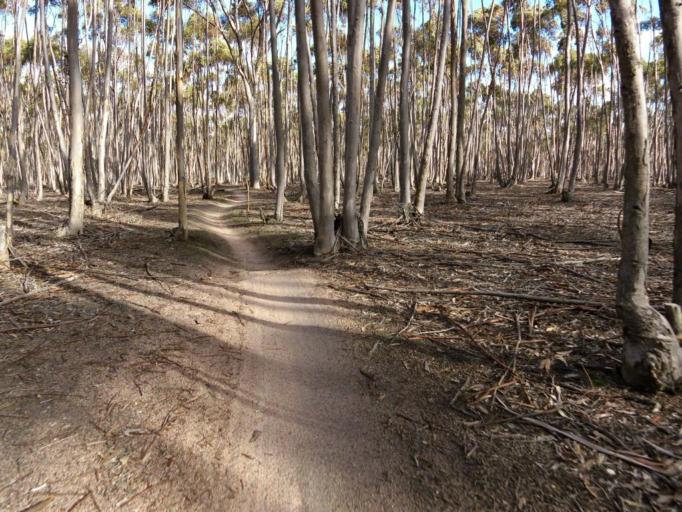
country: AU
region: Victoria
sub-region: Greater Geelong
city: Lara
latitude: -37.9411
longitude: 144.4025
